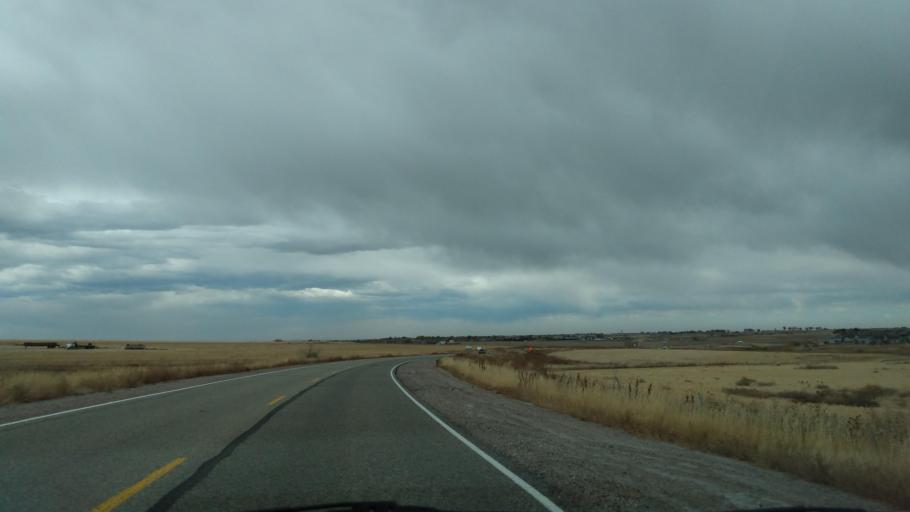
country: US
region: Colorado
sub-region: Adams County
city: Northglenn
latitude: 39.9718
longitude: -104.9752
